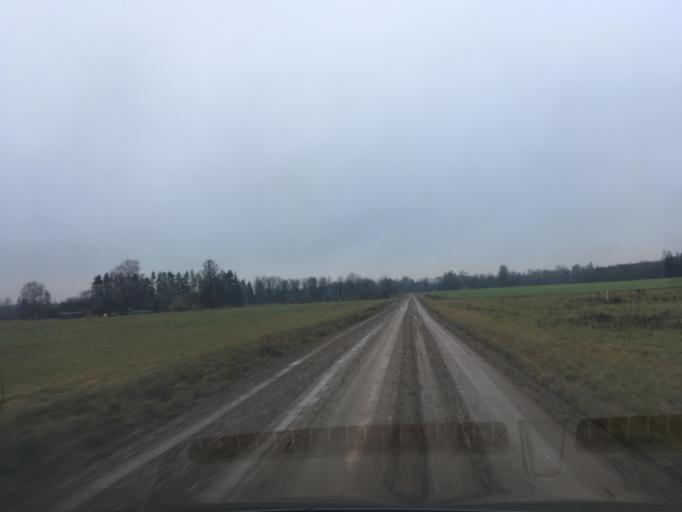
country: EE
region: Tartu
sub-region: Tartu linn
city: Tartu
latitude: 58.3881
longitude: 26.9278
